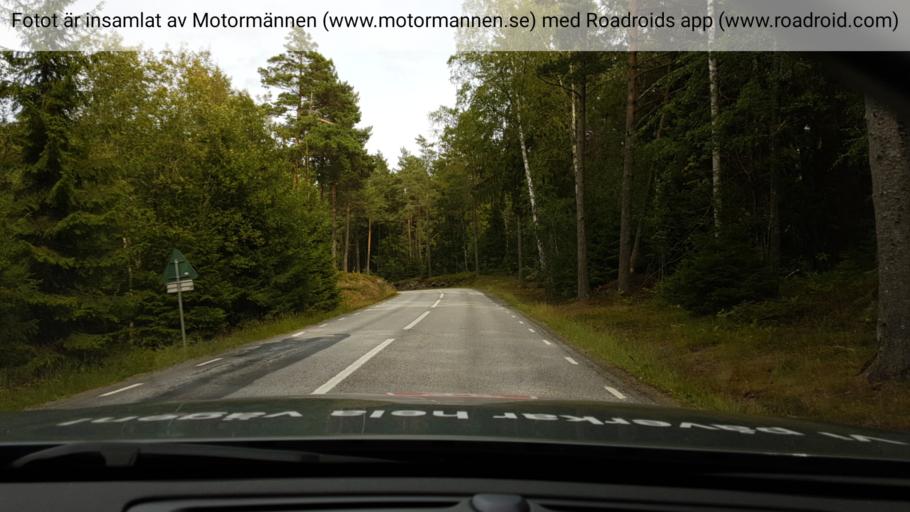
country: SE
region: Stockholm
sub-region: Botkyrka Kommun
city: Varsta
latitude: 59.1277
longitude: 17.8425
